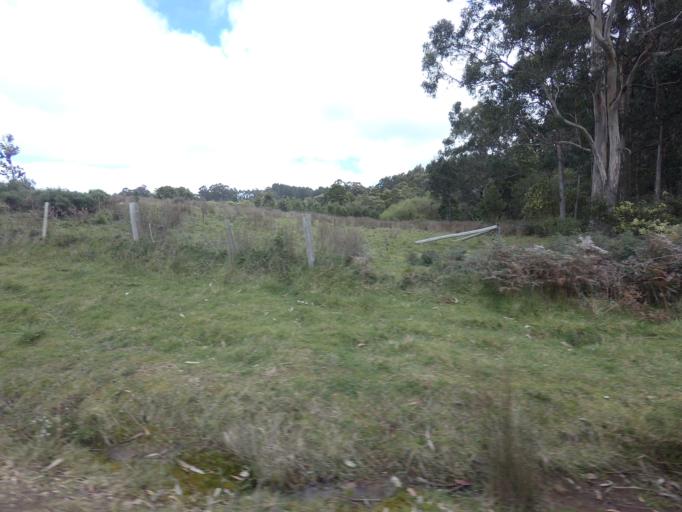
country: AU
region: Tasmania
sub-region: Huon Valley
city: Cygnet
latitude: -43.4079
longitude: 147.0178
